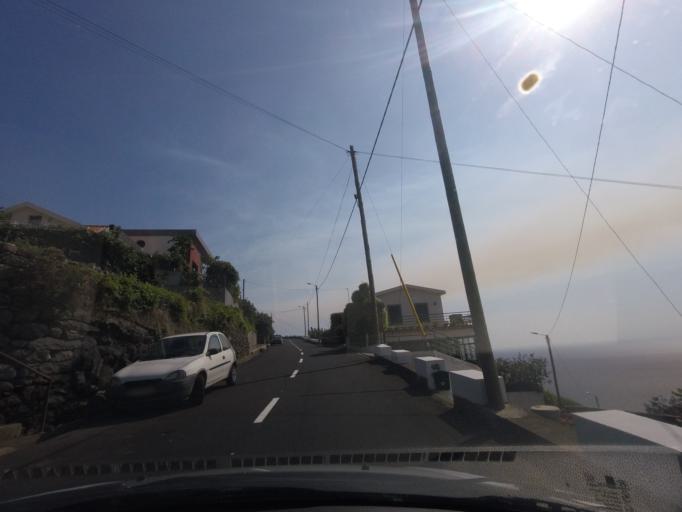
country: PT
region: Madeira
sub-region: Ribeira Brava
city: Campanario
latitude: 32.6684
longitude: -17.0527
